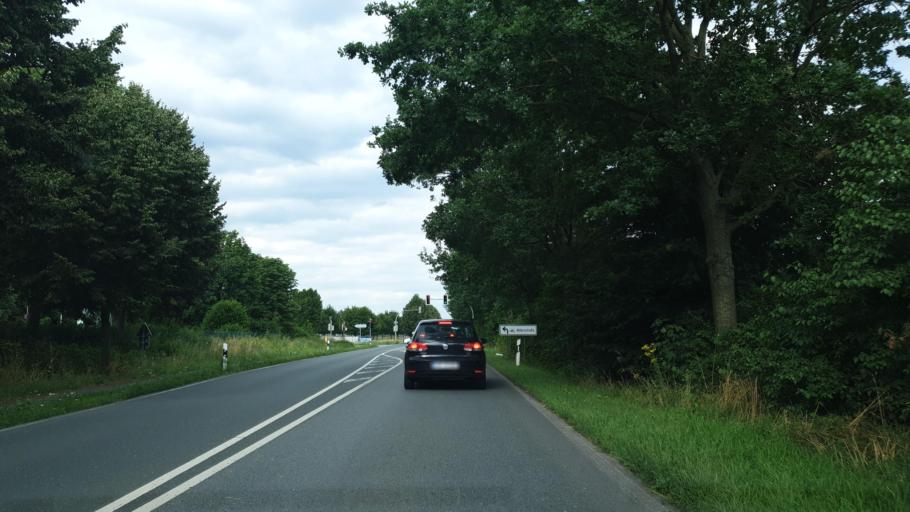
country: DE
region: North Rhine-Westphalia
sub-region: Regierungsbezirk Detmold
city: Herford
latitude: 52.0992
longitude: 8.6381
